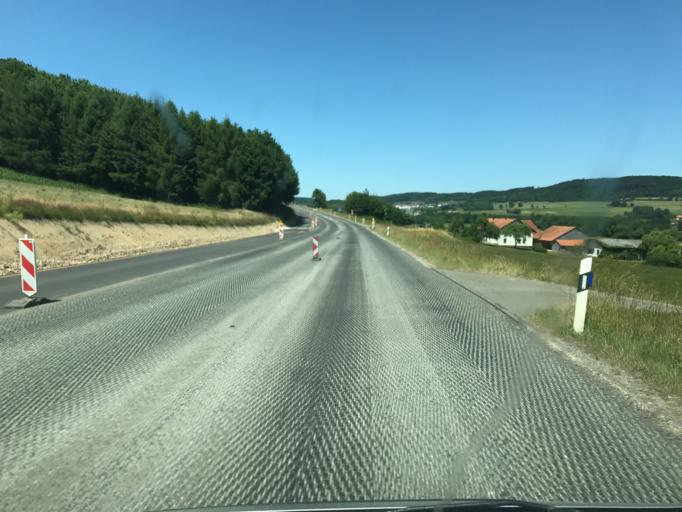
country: DE
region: Bavaria
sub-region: Upper Palatinate
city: Furth im Wald
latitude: 49.3273
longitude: 12.8468
